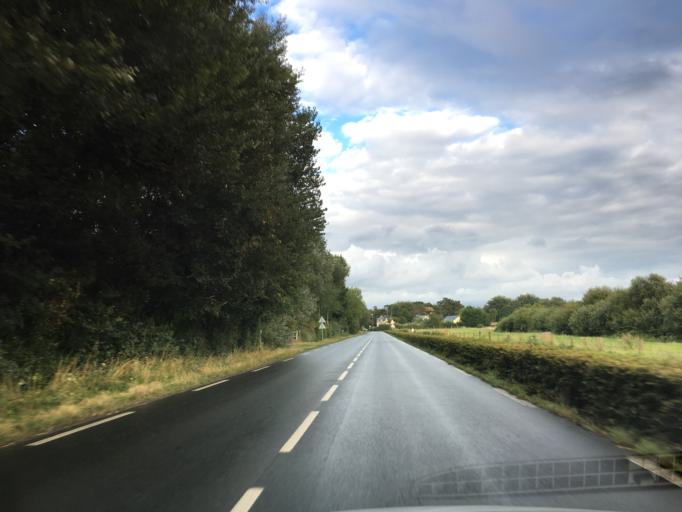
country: FR
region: Lower Normandy
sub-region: Departement du Calvados
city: Merville-Franceville-Plage
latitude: 49.2849
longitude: -0.1753
